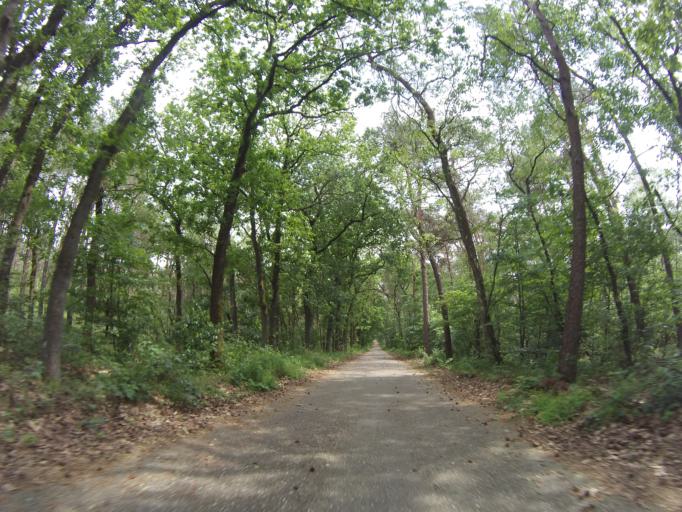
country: NL
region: Utrecht
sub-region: Gemeente Utrechtse Heuvelrug
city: Maarn
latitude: 52.0982
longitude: 5.3297
